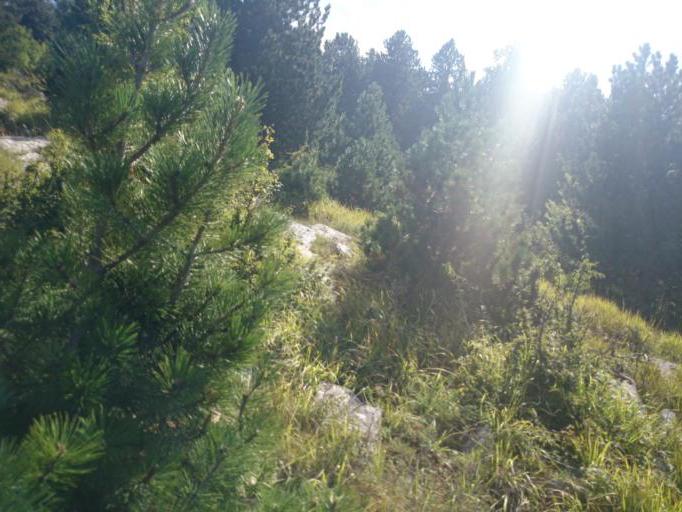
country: AL
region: Elbasan
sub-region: Rrethi i Gramshit
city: Kushove
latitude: 40.7418
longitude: 20.1509
